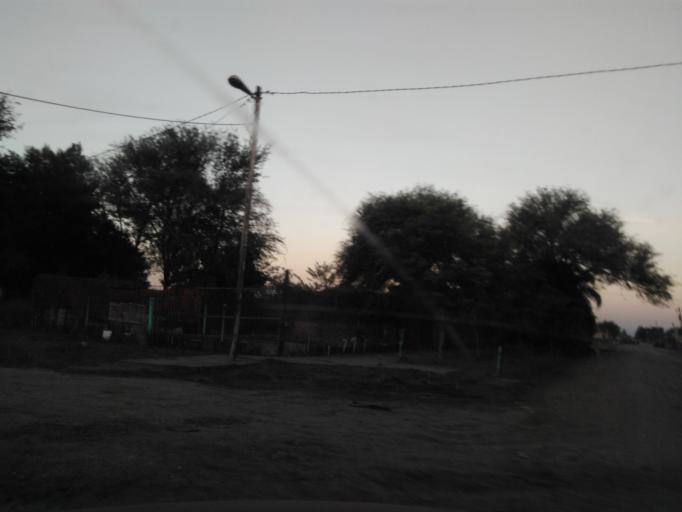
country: AR
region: Chaco
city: Resistencia
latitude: -27.4693
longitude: -59.0200
